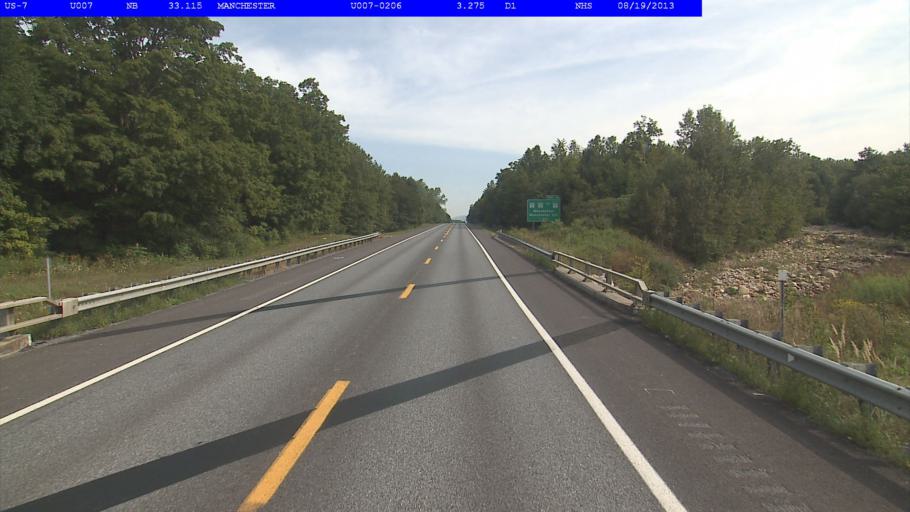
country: US
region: Vermont
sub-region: Bennington County
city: Manchester Center
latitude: 43.1565
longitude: -73.0442
